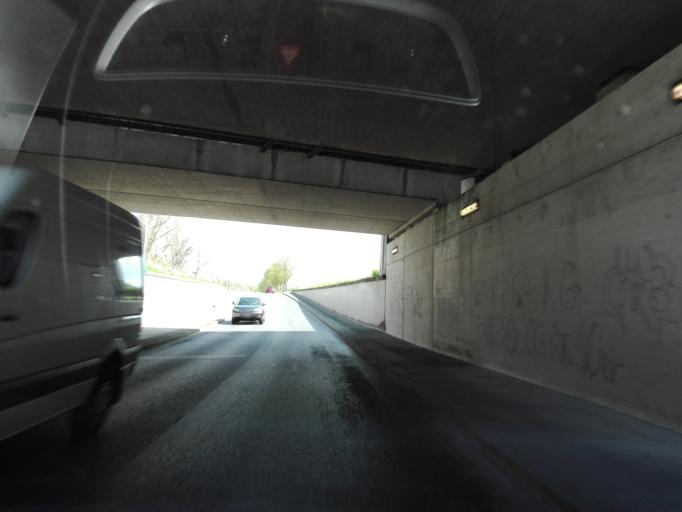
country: AT
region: Upper Austria
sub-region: Politischer Bezirk Linz-Land
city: Traun
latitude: 48.2323
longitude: 14.2590
